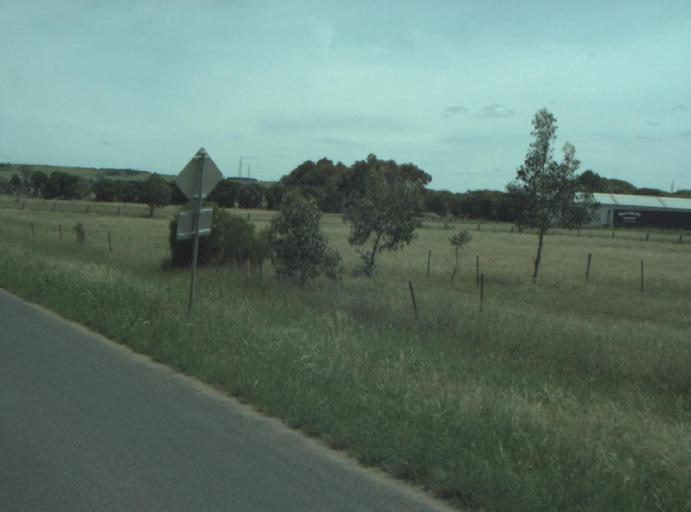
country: AU
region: Victoria
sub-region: Greater Geelong
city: Lara
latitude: -38.0217
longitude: 144.3755
